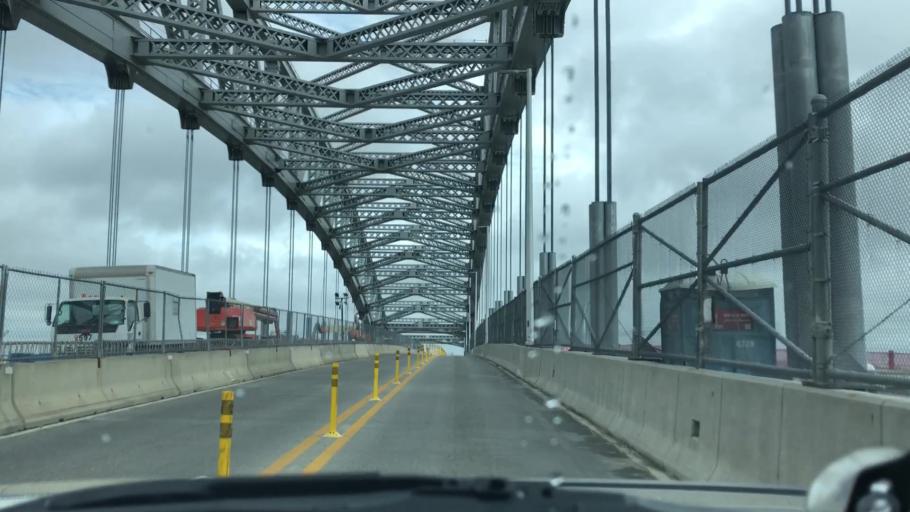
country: US
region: New Jersey
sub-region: Hudson County
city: Bayonne
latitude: 40.6413
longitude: -74.1425
